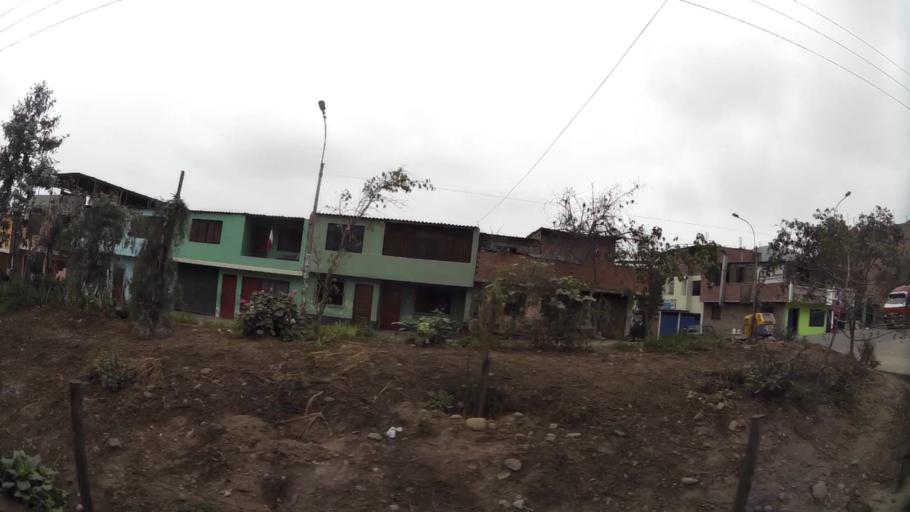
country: PE
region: Lima
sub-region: Lima
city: Surco
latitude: -12.1374
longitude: -76.9605
